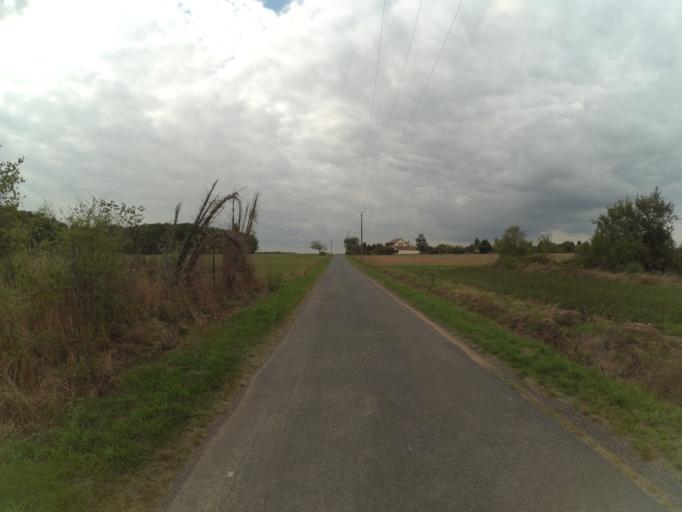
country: FR
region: Centre
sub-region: Departement d'Indre-et-Loire
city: Poce-sur-Cisse
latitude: 47.4984
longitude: 0.9812
